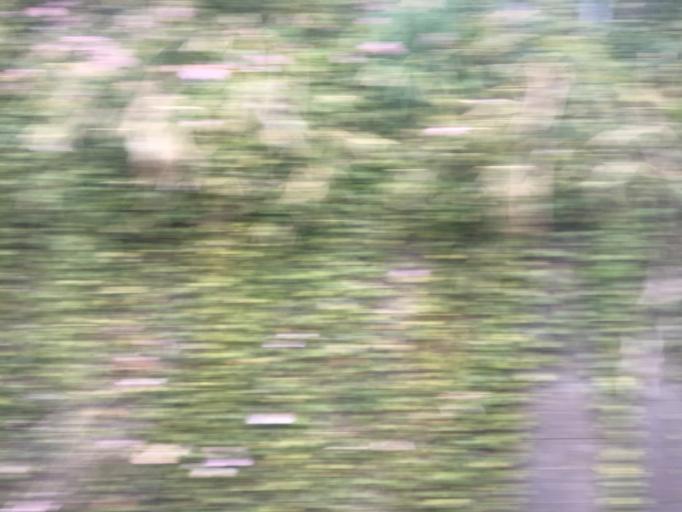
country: JP
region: Chiba
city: Oami
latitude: 35.5303
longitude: 140.2720
